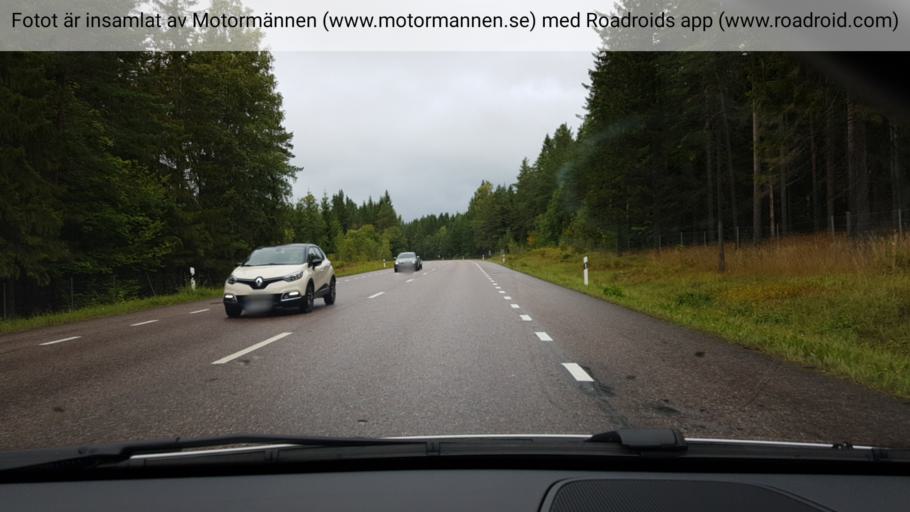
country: SE
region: Uppsala
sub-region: Alvkarleby Kommun
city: AElvkarleby
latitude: 60.5950
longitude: 17.4622
